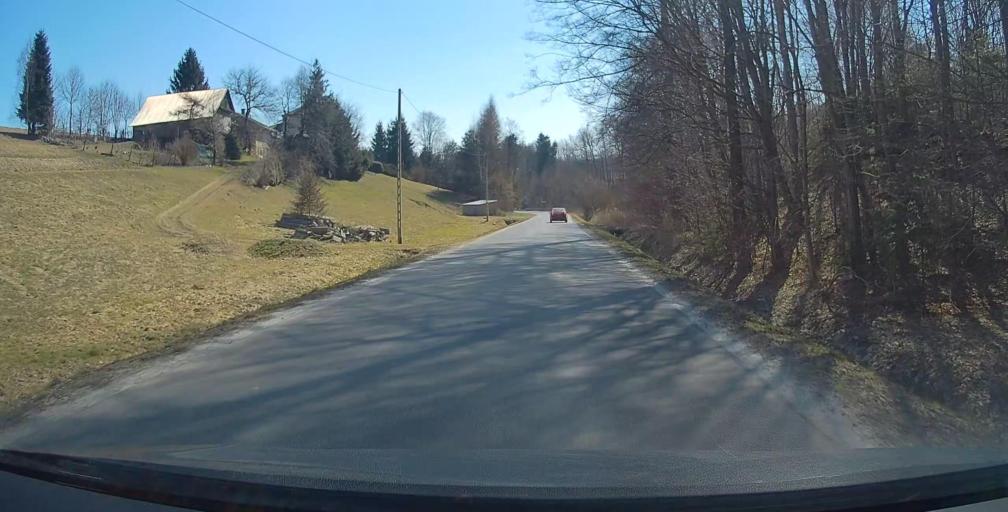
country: PL
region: Subcarpathian Voivodeship
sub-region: Powiat rzeszowski
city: Hyzne
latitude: 49.8933
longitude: 22.2237
